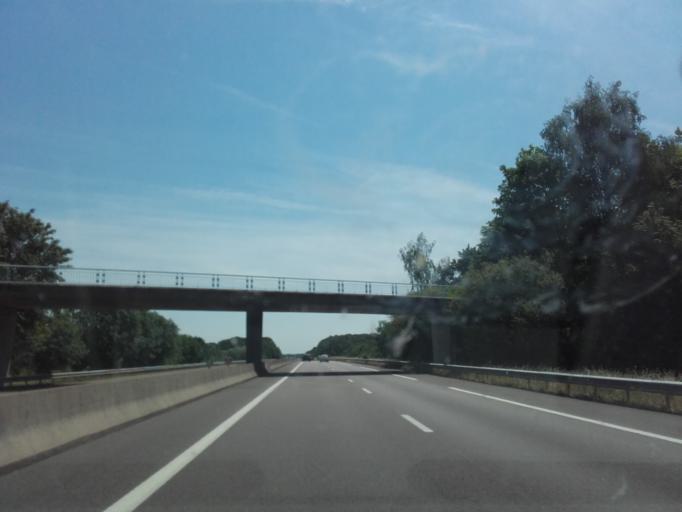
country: FR
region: Bourgogne
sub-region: Departement de la Cote-d'Or
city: Semur-en-Auxois
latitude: 47.4733
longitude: 4.2107
